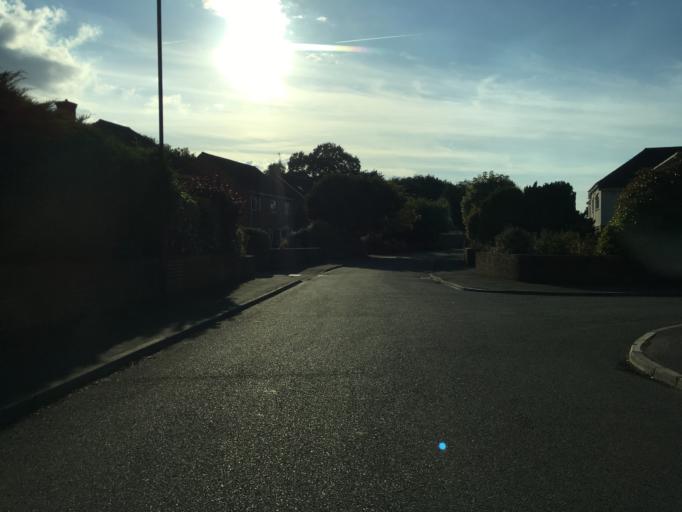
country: GB
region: England
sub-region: South Gloucestershire
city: Mangotsfield
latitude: 51.4994
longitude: -2.5192
